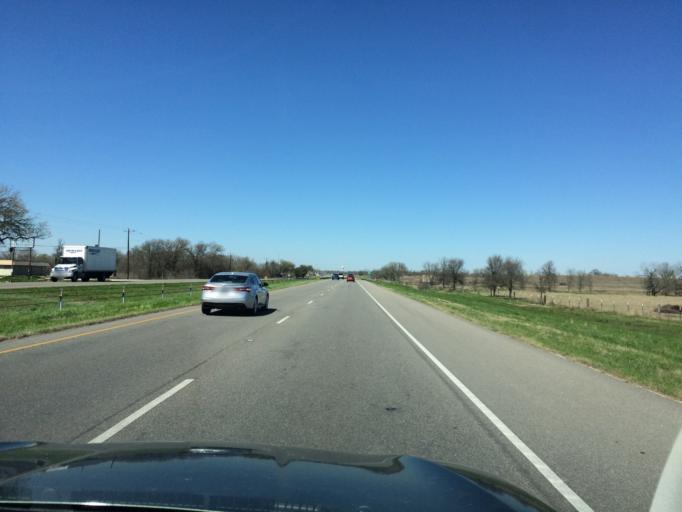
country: US
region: Texas
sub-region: Travis County
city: Garfield
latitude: 30.1783
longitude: -97.5326
